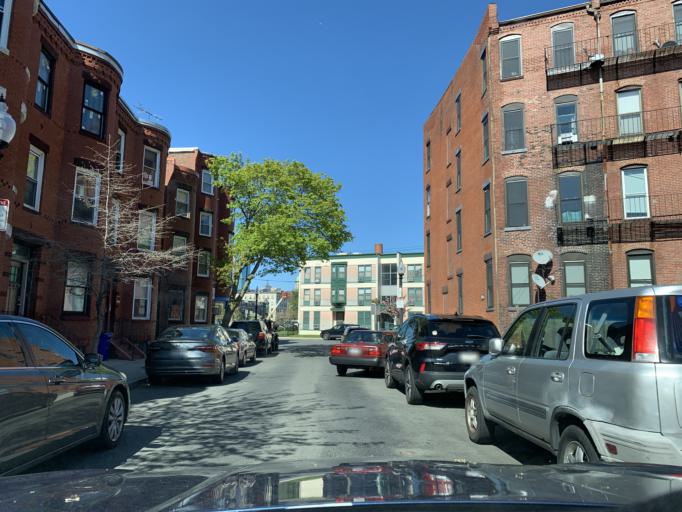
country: US
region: Massachusetts
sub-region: Suffolk County
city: Boston
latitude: 42.3364
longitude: -71.0840
